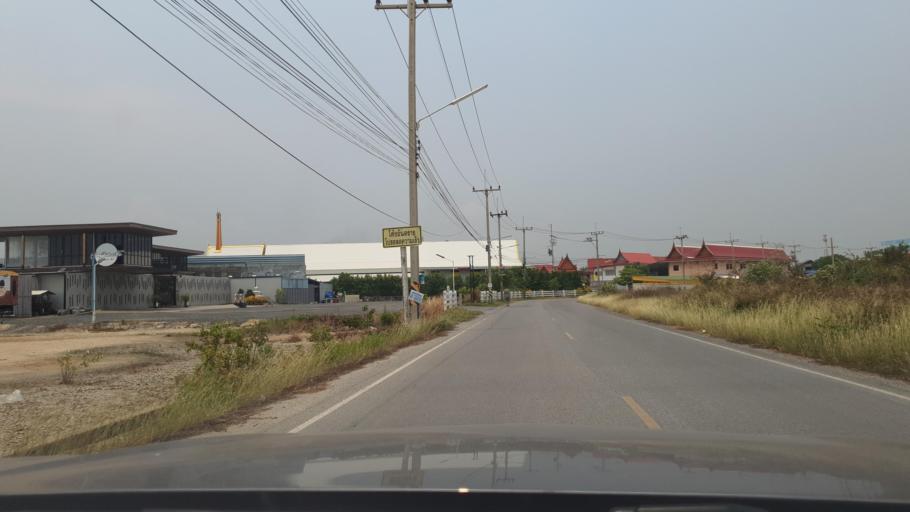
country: TH
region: Chachoengsao
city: Bang Pakong
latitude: 13.4888
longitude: 101.0164
